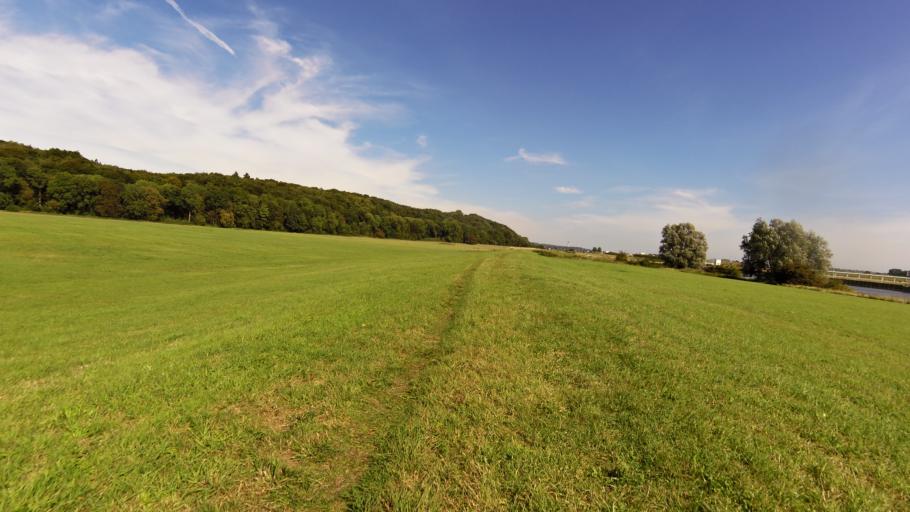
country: NL
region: Gelderland
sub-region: Gemeente Renkum
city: Doorwerth
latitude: 51.9658
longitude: 5.7973
